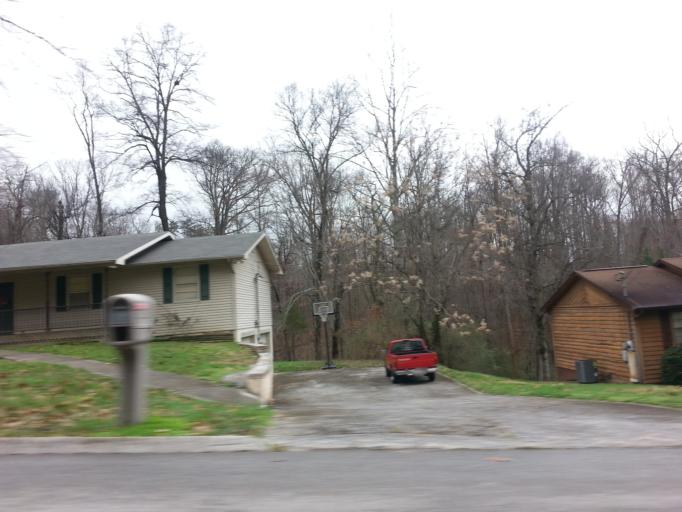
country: US
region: Tennessee
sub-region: Knox County
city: Knoxville
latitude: 35.9903
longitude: -84.0188
